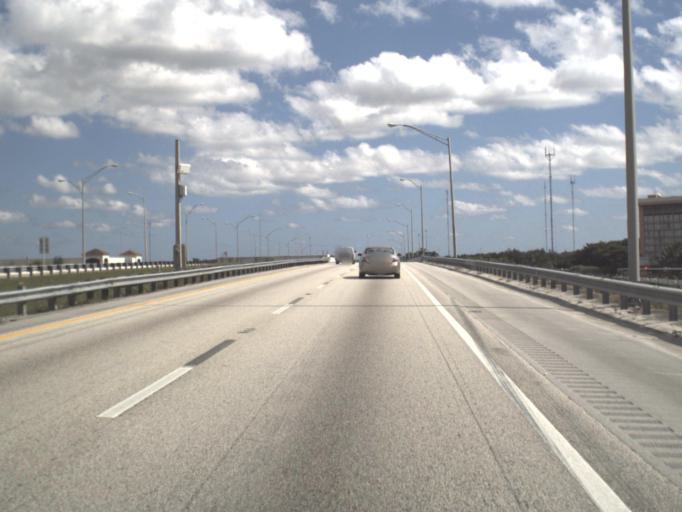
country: US
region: Florida
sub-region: Miami-Dade County
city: Lake Lucerne
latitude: 25.9722
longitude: -80.2486
